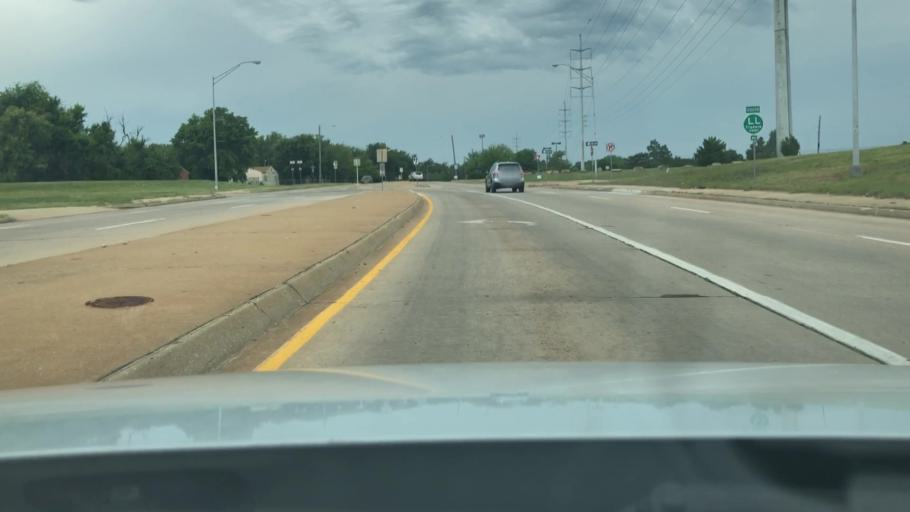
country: US
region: Oklahoma
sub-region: Tulsa County
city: Tulsa
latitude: 36.1770
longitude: -96.0013
